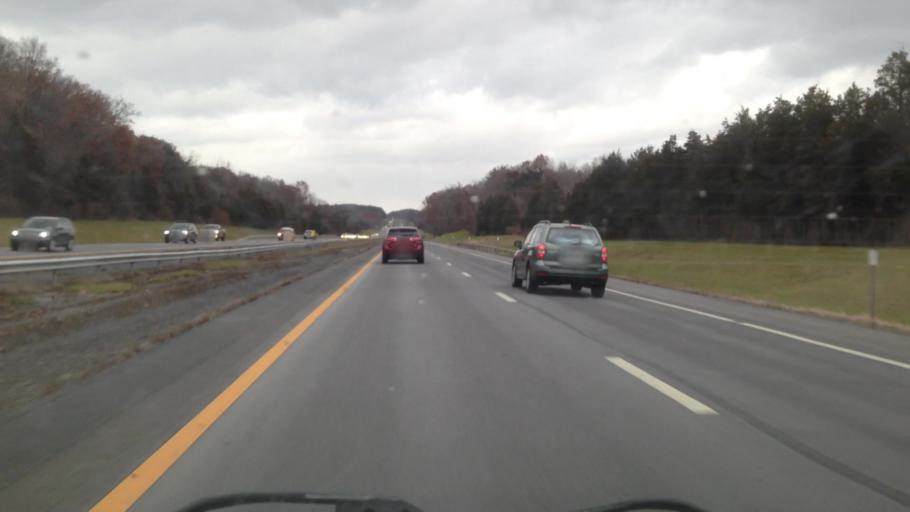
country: US
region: New York
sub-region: Greene County
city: Palenville
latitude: 42.1652
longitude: -73.9360
